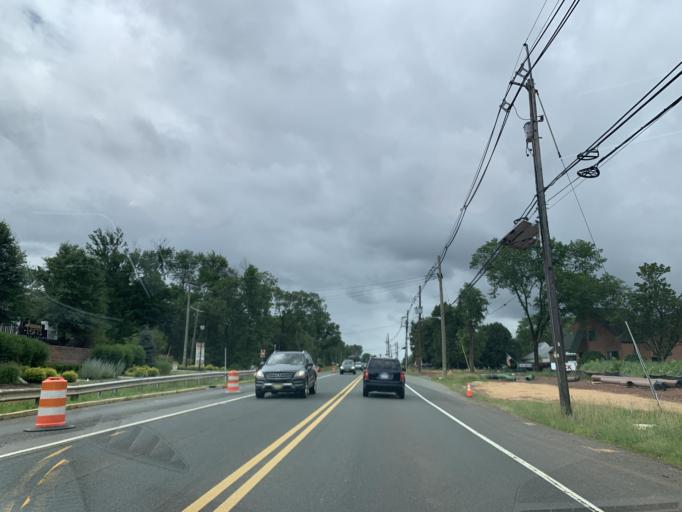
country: US
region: New Jersey
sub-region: Somerset County
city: Bloomingdale
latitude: 40.5263
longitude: -74.6272
